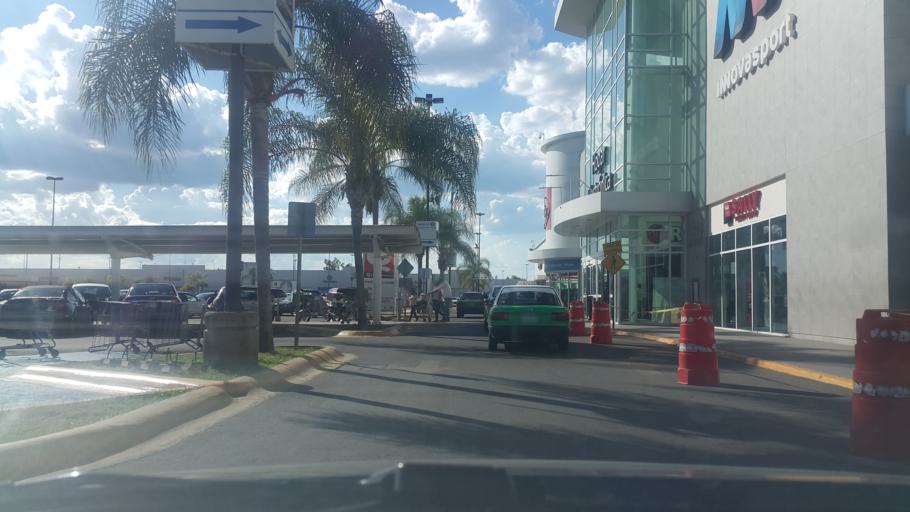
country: MX
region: Guanajuato
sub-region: Leon
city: Medina
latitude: 21.1466
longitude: -101.6470
